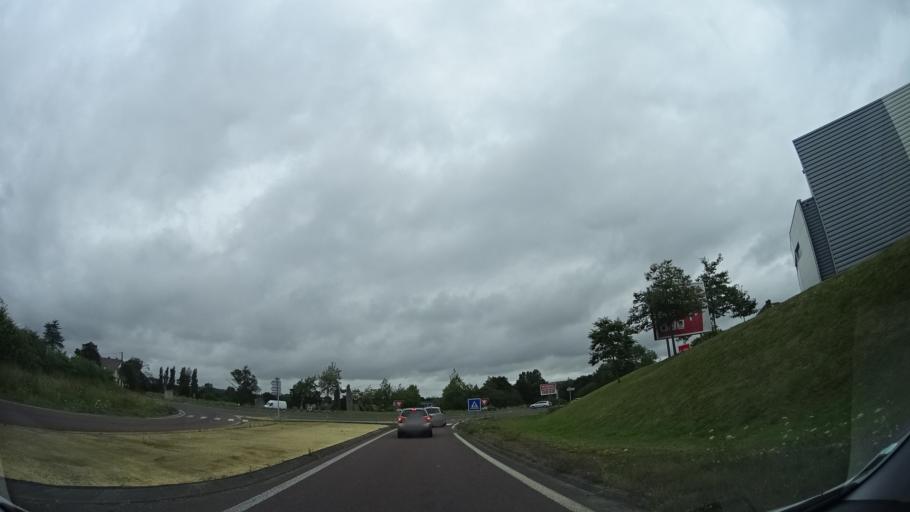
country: FR
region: Lower Normandy
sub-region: Departement de la Manche
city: La Haye-du-Puits
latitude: 49.2943
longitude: -1.5581
